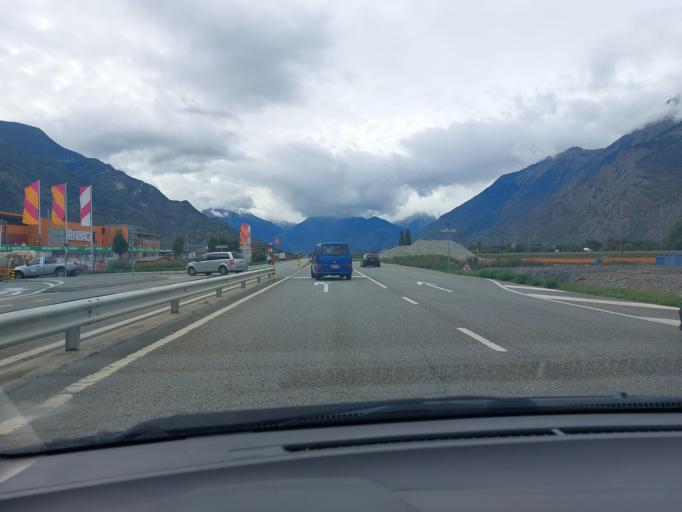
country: CH
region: Valais
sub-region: Martigny District
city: Riddes
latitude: 46.1666
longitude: 7.2116
